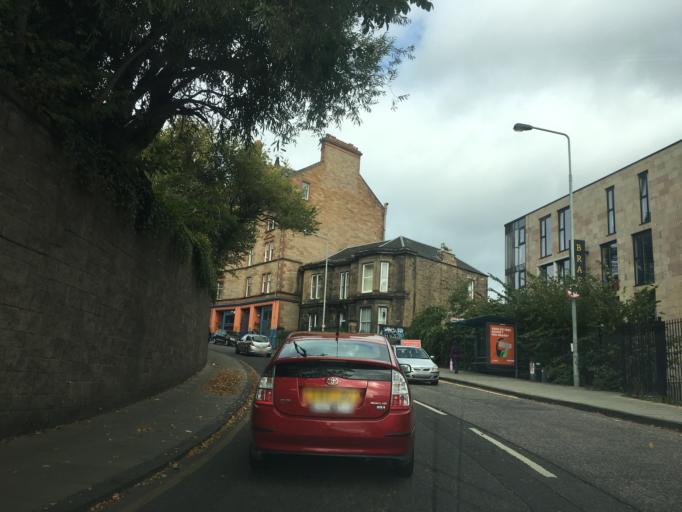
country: GB
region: Scotland
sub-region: West Lothian
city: Seafield
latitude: 55.9557
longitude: -3.1720
